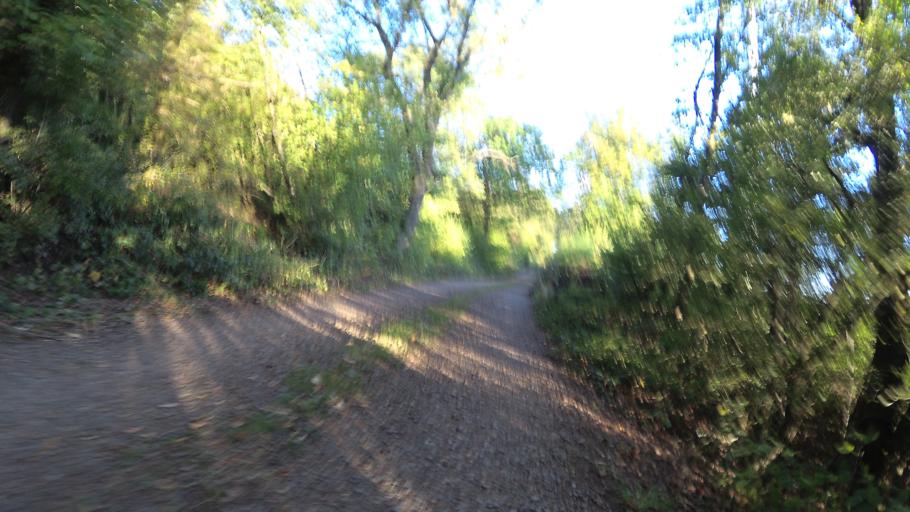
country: DE
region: Rheinland-Pfalz
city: Breitenbach
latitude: 49.4376
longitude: 7.2162
